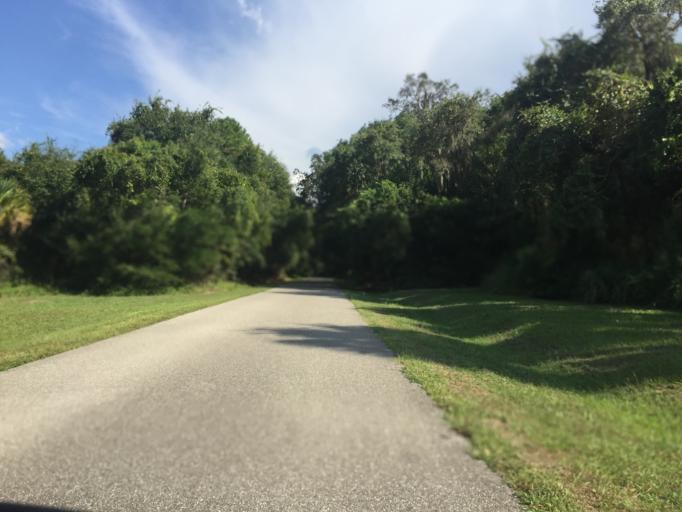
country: US
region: Florida
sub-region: Seminole County
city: Oviedo
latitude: 28.6879
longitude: -81.2560
